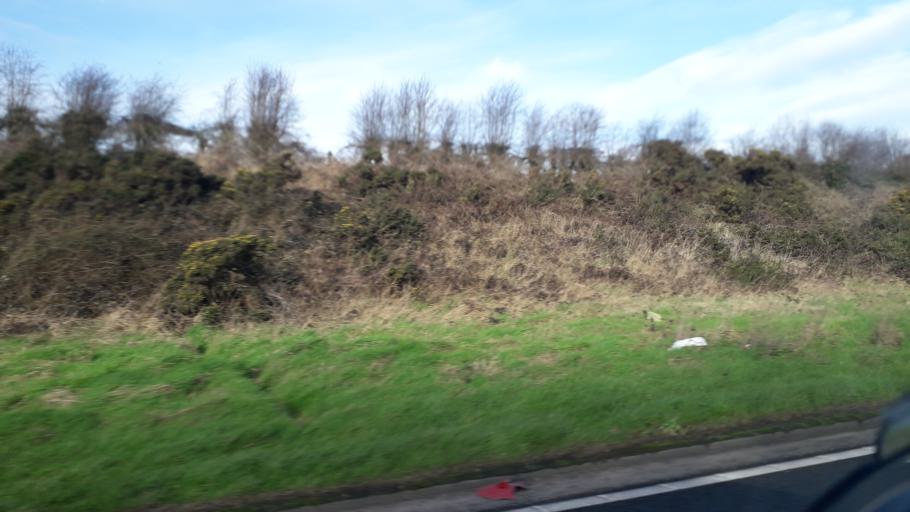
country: GB
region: Northern Ireland
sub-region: Banbridge District
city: Banbridge
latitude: 54.3500
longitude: -6.2410
